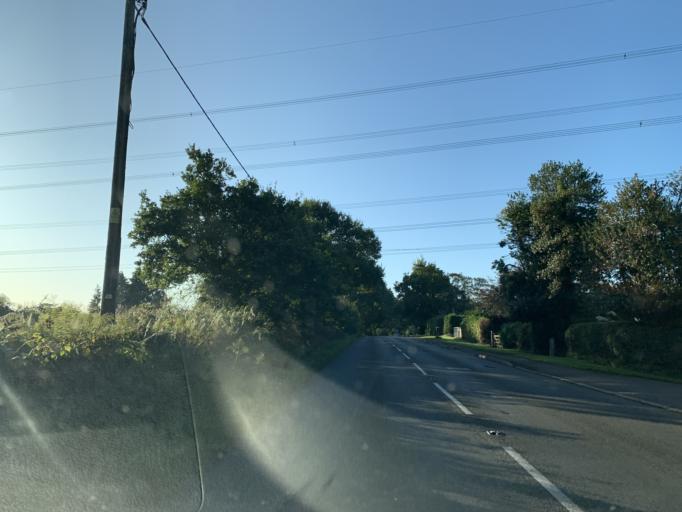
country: GB
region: England
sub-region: Wiltshire
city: Whiteparish
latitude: 50.9636
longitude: -1.6327
